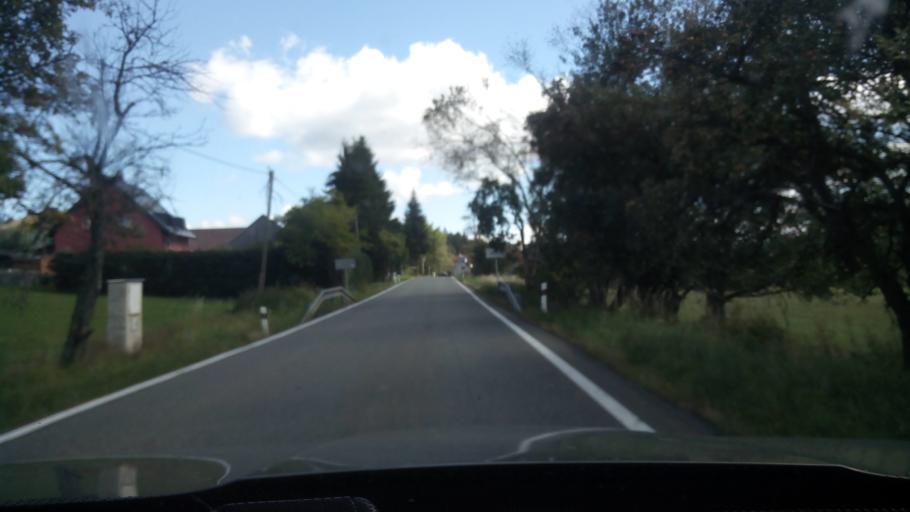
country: CZ
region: Jihocesky
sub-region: Okres Prachatice
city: Stachy
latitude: 49.1249
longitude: 13.6178
